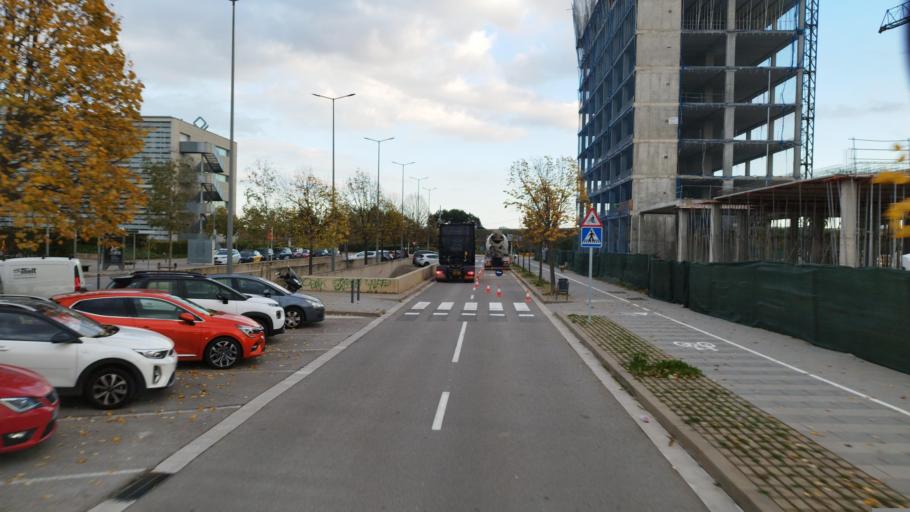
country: ES
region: Catalonia
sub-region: Provincia de Barcelona
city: Viladecans
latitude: 41.3136
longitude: 2.0298
